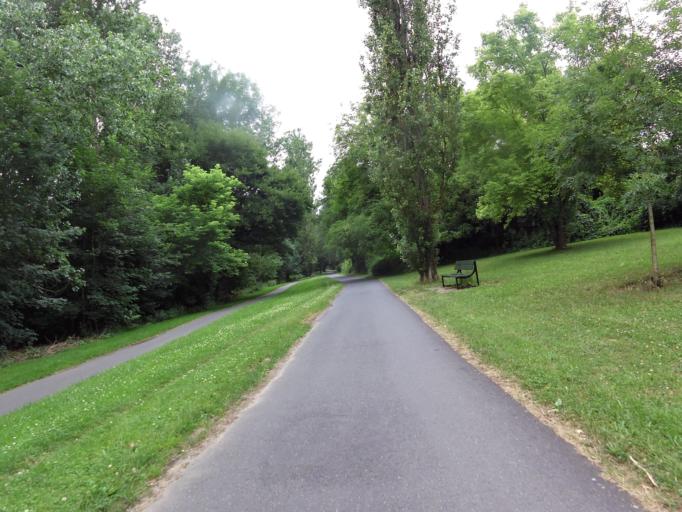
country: DE
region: Bavaria
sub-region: Regierungsbezirk Unterfranken
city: Wuerzburg
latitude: 49.7682
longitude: 9.9528
